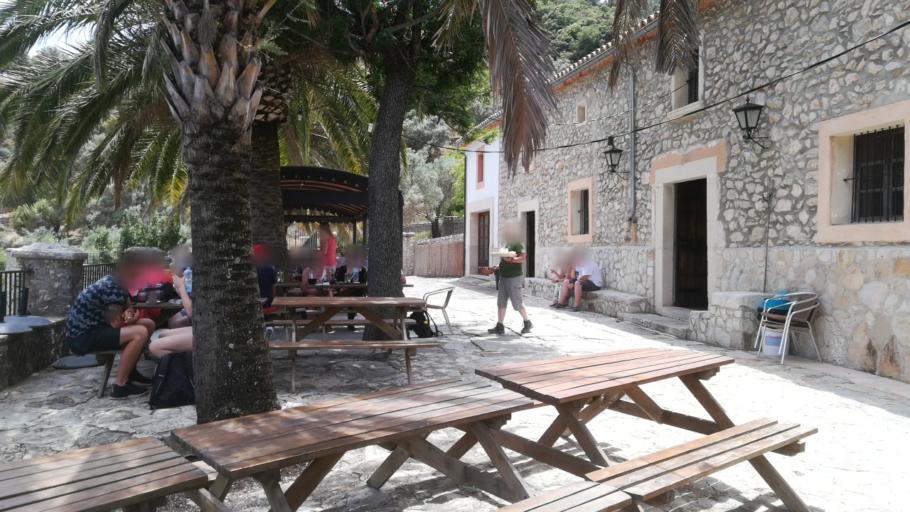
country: ES
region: Balearic Islands
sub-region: Illes Balears
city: Mancor de la Vall
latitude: 39.7617
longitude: 2.8624
